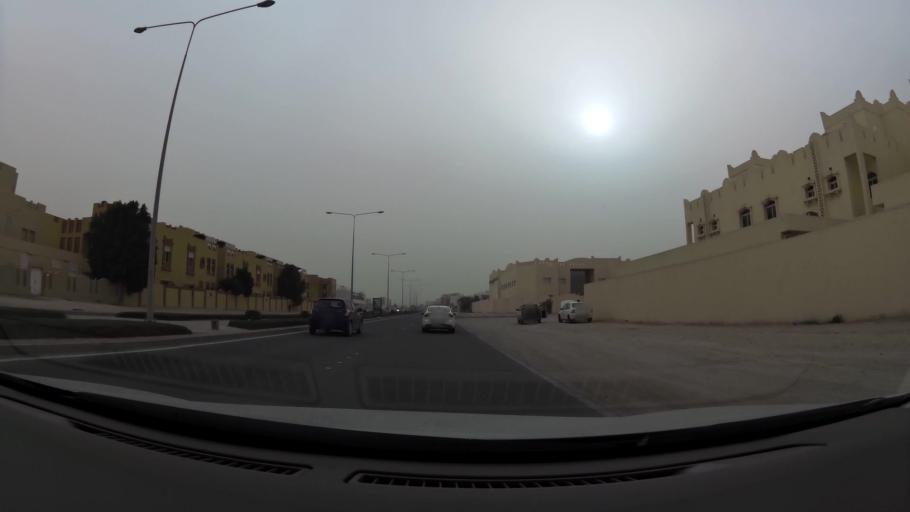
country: QA
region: Baladiyat ad Dawhah
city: Doha
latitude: 25.2501
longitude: 51.4844
